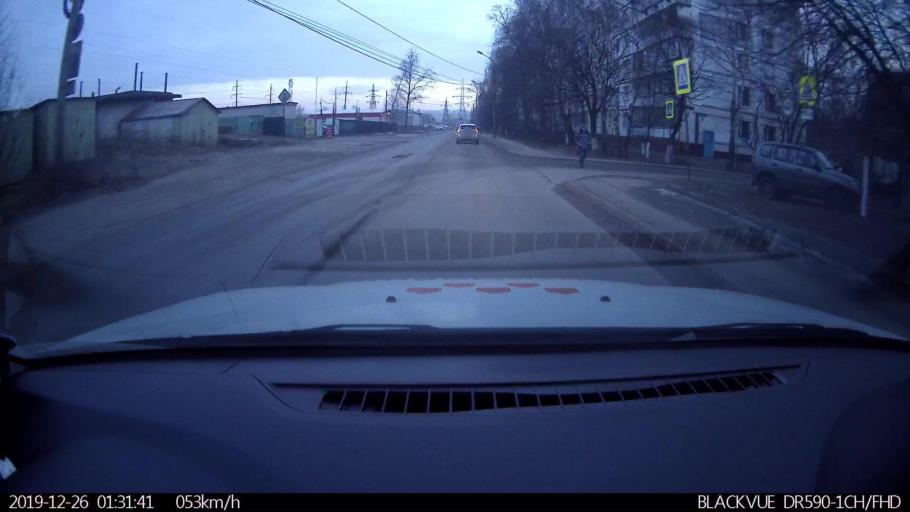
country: RU
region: Nizjnij Novgorod
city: Nizhniy Novgorod
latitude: 56.2660
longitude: 43.9010
